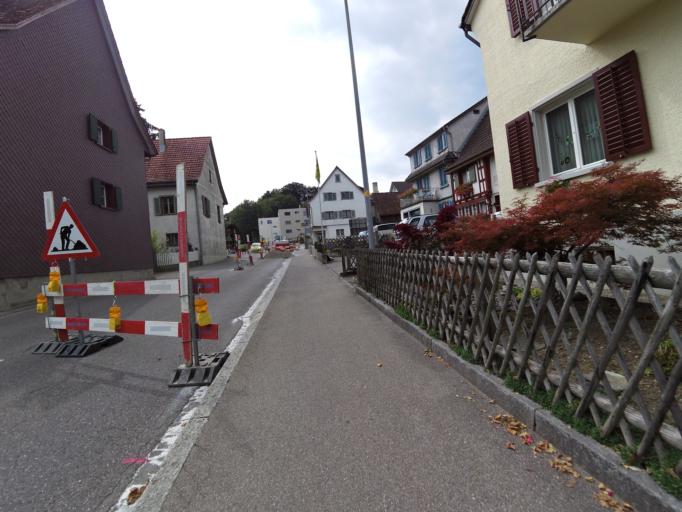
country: CH
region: Thurgau
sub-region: Kreuzlingen District
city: Ermatingen
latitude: 47.6681
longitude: 9.0802
